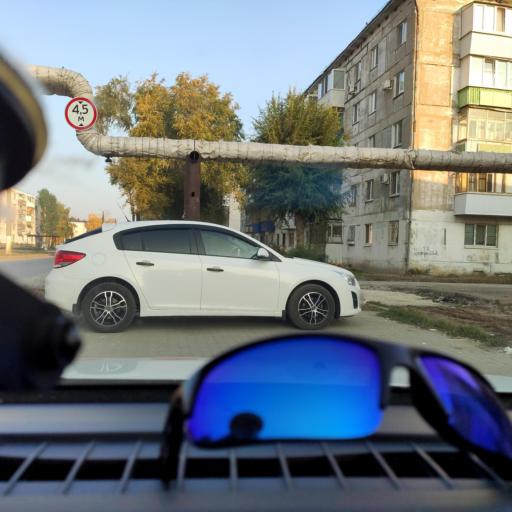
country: RU
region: Samara
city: Chapayevsk
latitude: 52.9509
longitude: 49.6958
